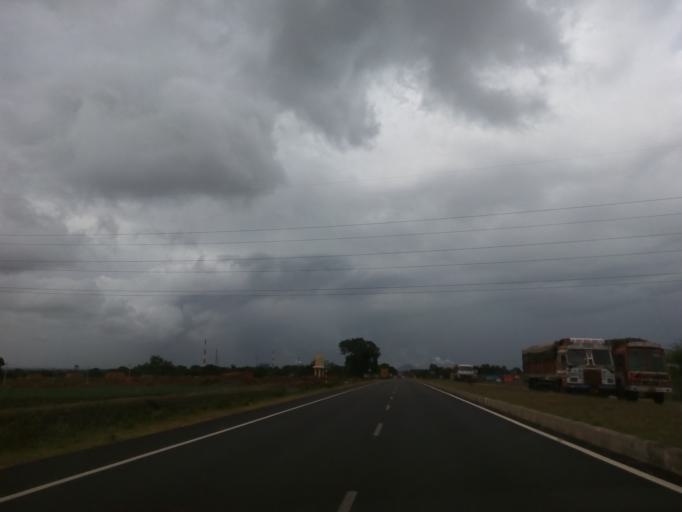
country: IN
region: Karnataka
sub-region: Davanagere
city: Harihar
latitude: 14.5389
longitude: 75.7589
